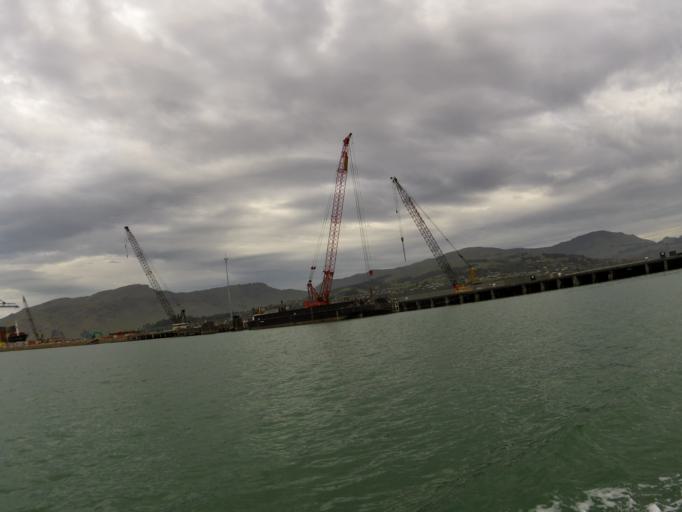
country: NZ
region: Canterbury
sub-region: Christchurch City
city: Christchurch
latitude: -43.6085
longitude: 172.7186
